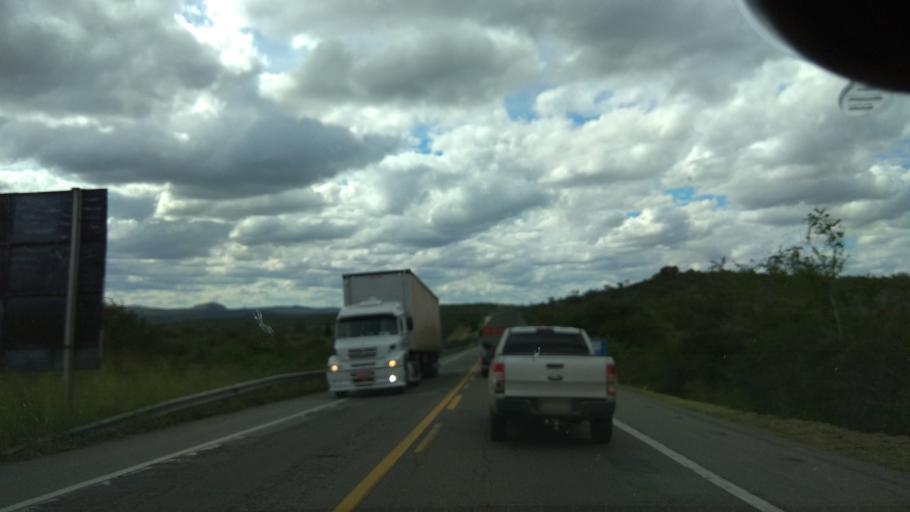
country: BR
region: Bahia
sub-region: Santa Ines
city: Santa Ines
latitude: -13.0046
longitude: -39.9559
